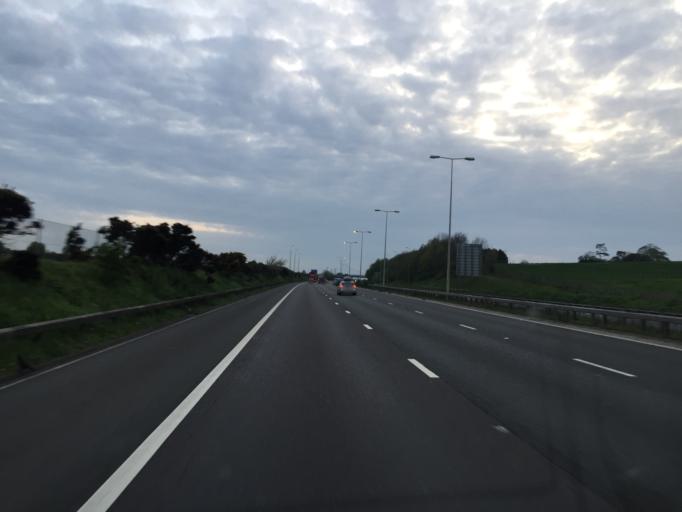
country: GB
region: England
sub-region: Kent
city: Hythe
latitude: 51.0921
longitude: 1.0894
